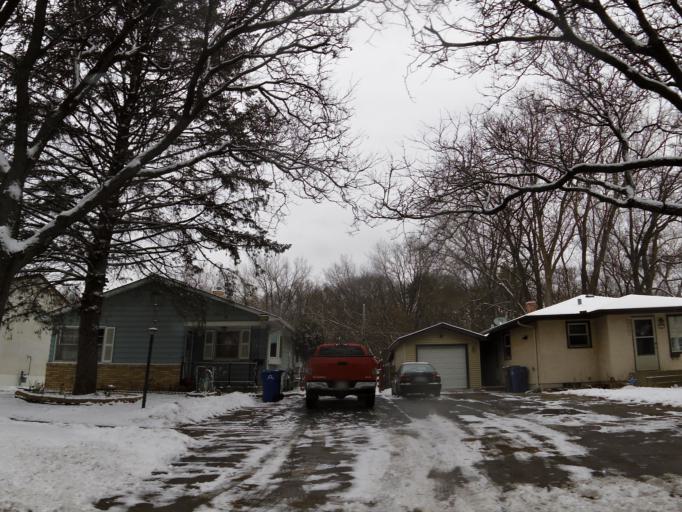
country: US
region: Minnesota
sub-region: Ramsey County
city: Maplewood
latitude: 44.9568
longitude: -93.0213
